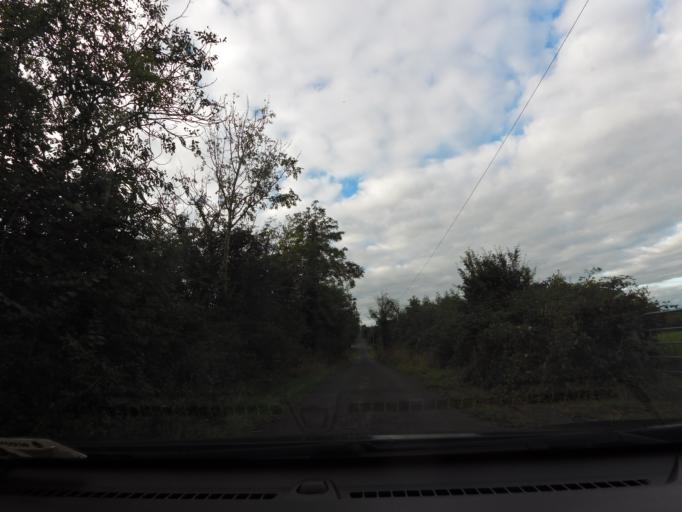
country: IE
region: Connaught
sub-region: County Galway
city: Loughrea
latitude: 53.1481
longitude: -8.5165
